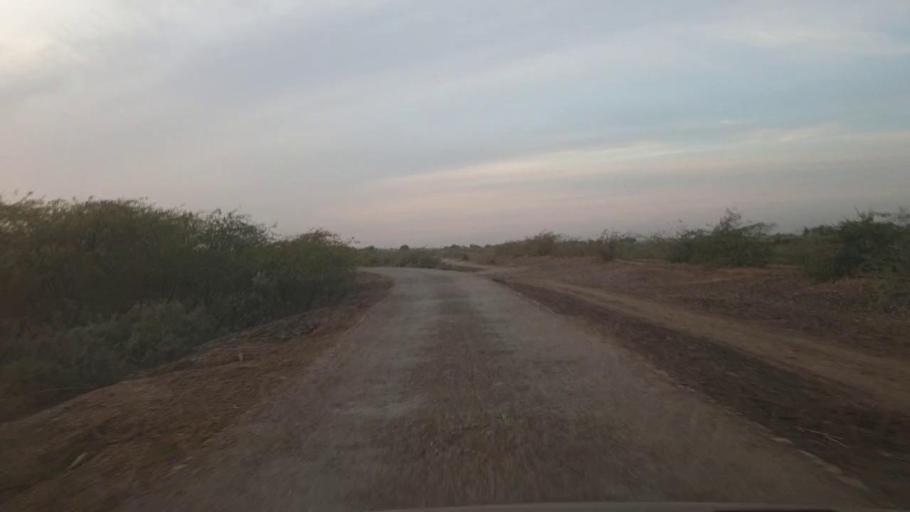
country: PK
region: Sindh
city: Kunri
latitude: 25.2324
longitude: 69.5302
